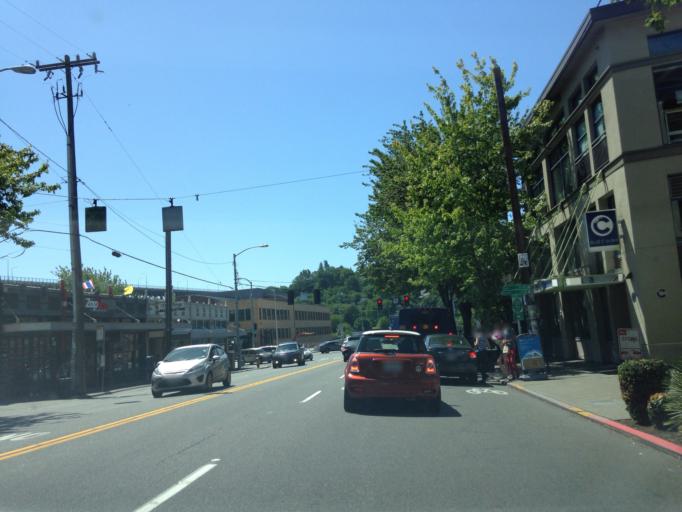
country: US
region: Washington
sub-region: King County
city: Seattle
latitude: 47.6502
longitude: -122.3499
